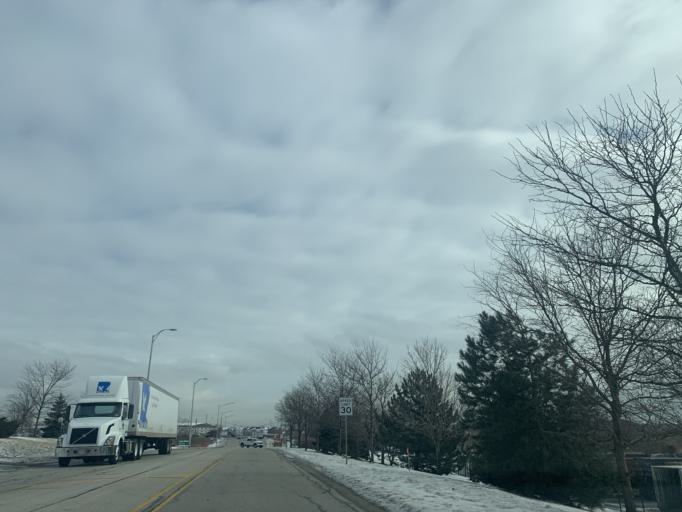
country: US
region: Illinois
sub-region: Will County
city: Romeoville
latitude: 41.6522
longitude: -88.1299
